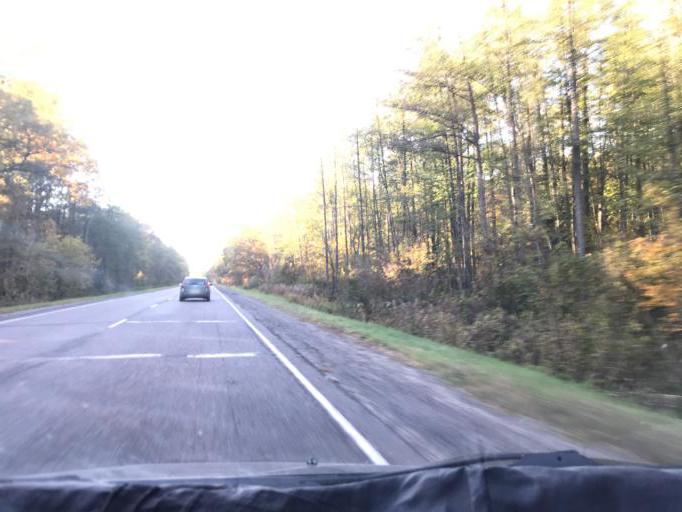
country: BY
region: Gomel
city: Pyetrykaw
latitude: 52.2697
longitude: 28.2825
